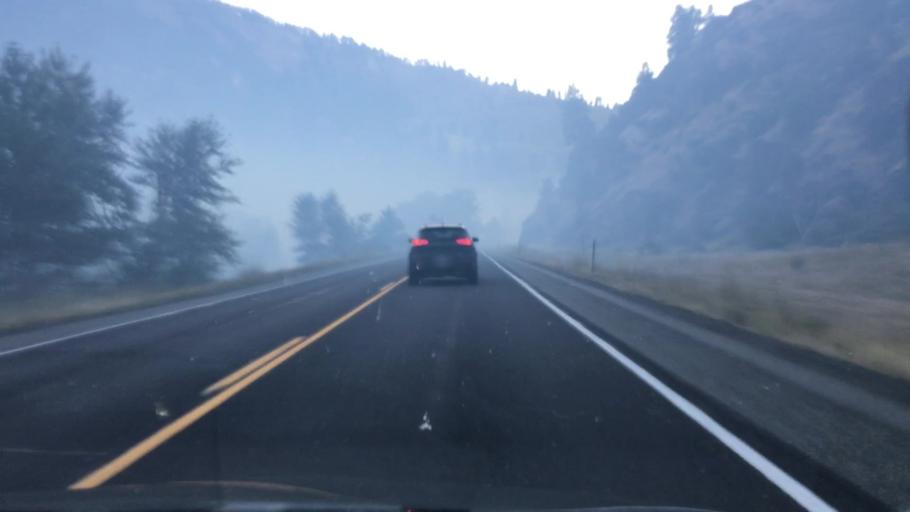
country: US
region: Idaho
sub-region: Valley County
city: McCall
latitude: 45.2844
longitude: -116.3502
